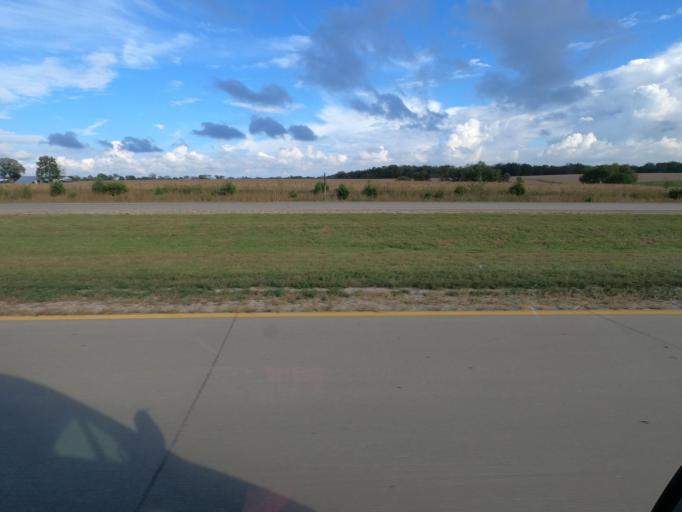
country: US
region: Illinois
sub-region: Hancock County
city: Nauvoo
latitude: 40.5880
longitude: -91.5642
